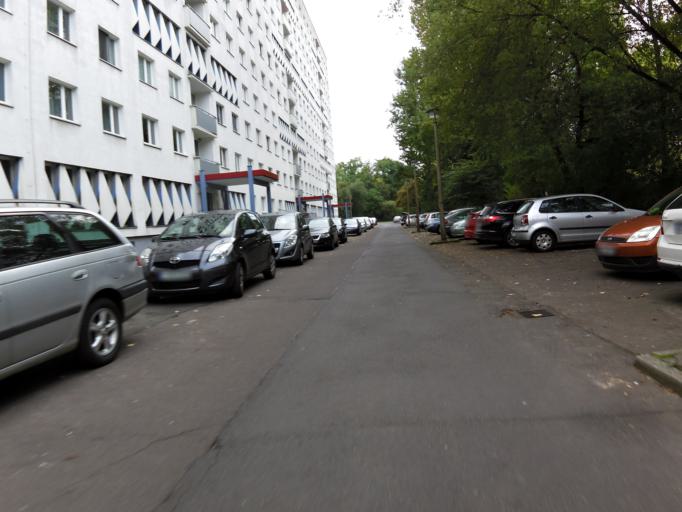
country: DE
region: Saxony
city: Leipzig
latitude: 51.3231
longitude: 12.3902
